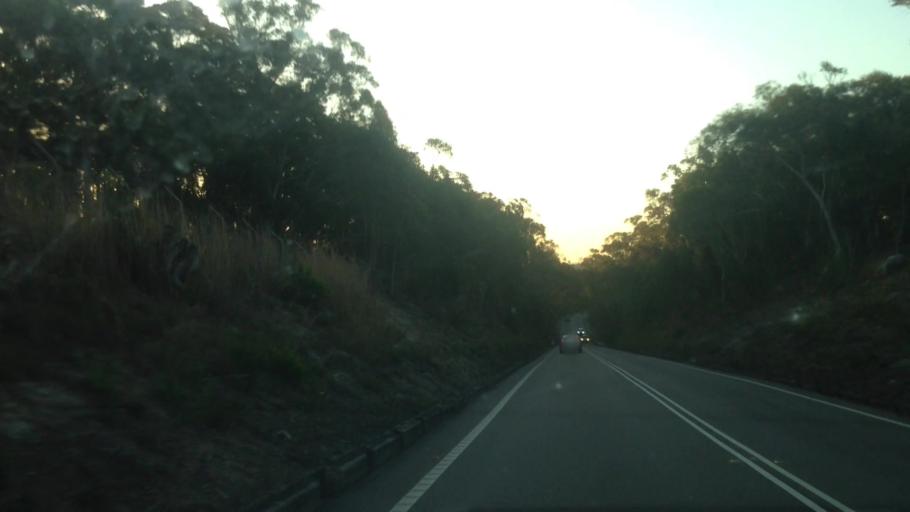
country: AU
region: New South Wales
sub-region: Wyong Shire
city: Kingfisher Shores
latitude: -33.1635
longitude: 151.5319
